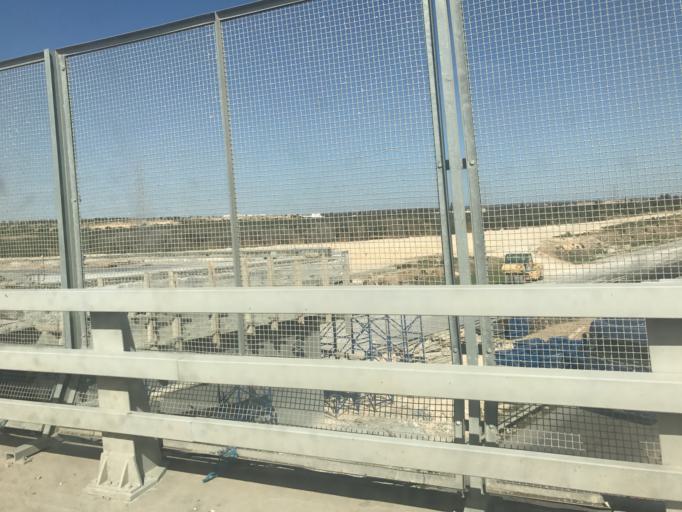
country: TN
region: Susah
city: Masakin
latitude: 35.7760
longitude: 10.5572
